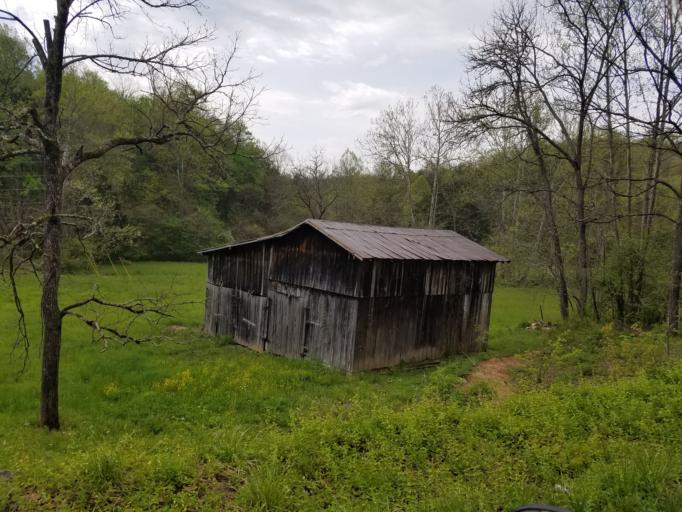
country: US
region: Kentucky
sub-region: Harlan County
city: Harlan
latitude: 36.6943
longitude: -83.2870
